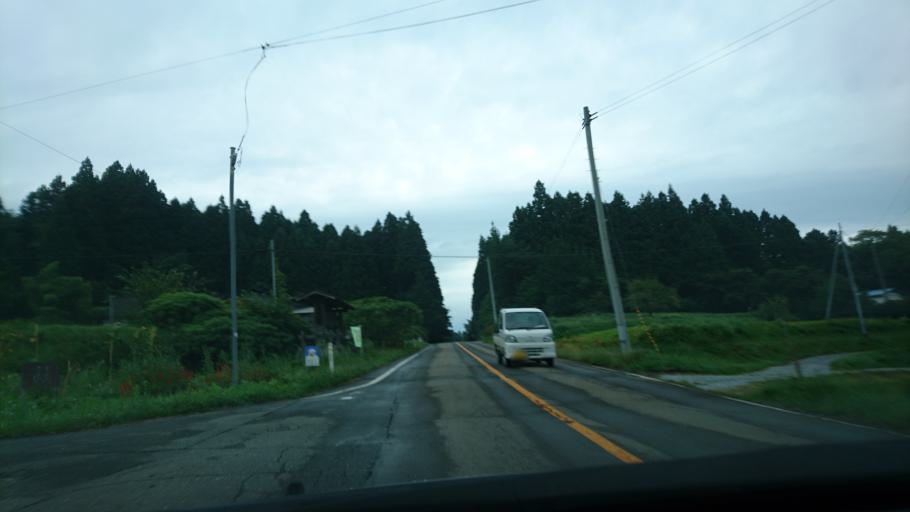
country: JP
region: Iwate
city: Ichinoseki
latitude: 39.0223
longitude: 141.2035
